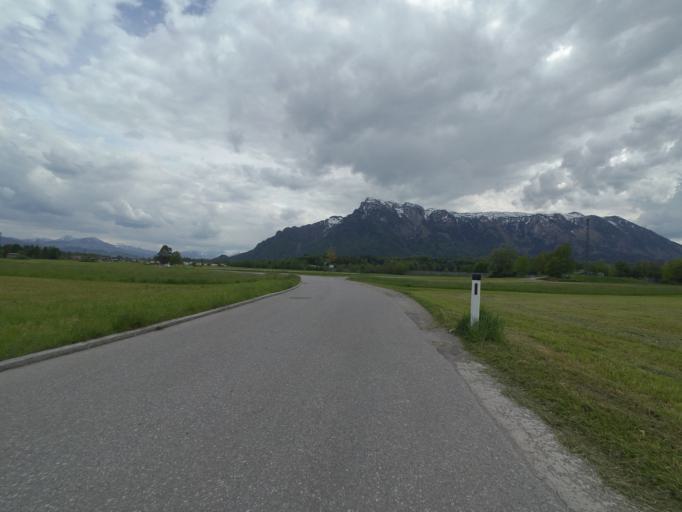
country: AT
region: Salzburg
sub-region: Politischer Bezirk Salzburg-Umgebung
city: Grodig
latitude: 47.7701
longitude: 12.9917
